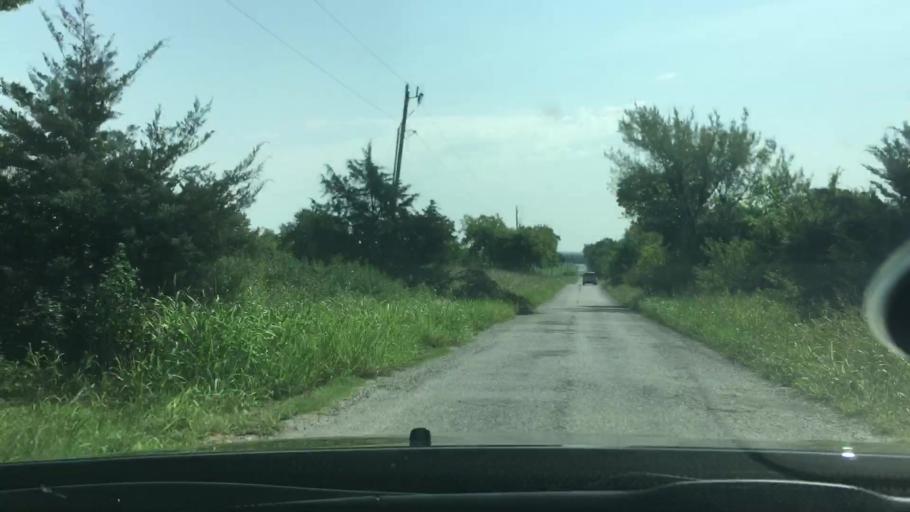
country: US
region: Oklahoma
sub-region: Bryan County
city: Durant
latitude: 34.0557
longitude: -96.3711
